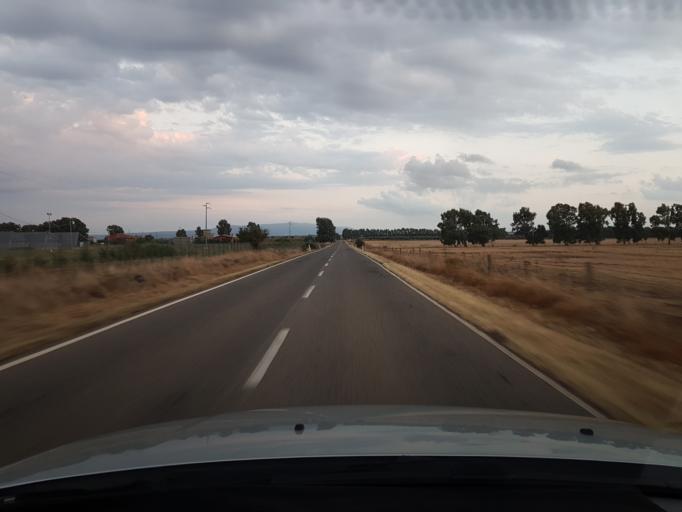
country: IT
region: Sardinia
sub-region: Provincia di Oristano
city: Milis
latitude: 40.0289
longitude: 8.6400
